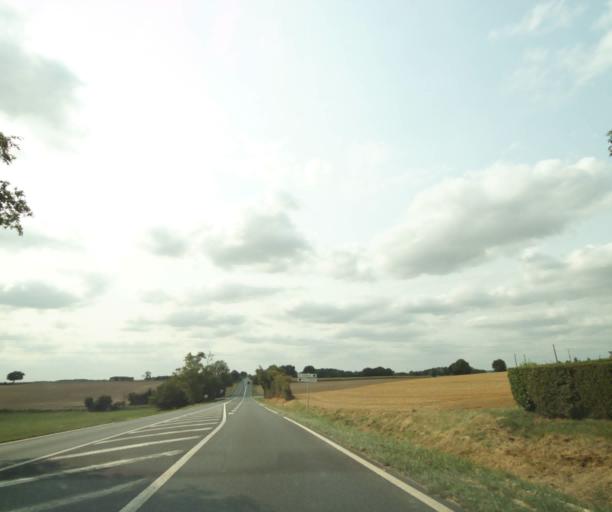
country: FR
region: Centre
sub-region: Departement de l'Indre
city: Buzancais
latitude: 46.9079
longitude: 1.3450
